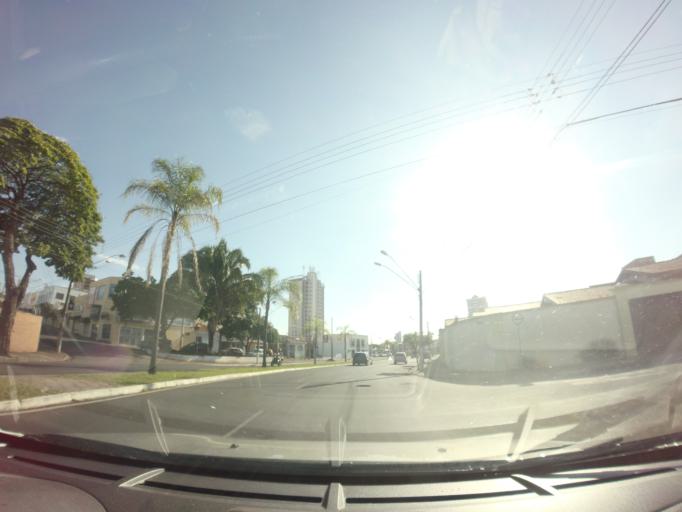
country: BR
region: Sao Paulo
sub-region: Rio Claro
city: Rio Claro
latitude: -22.4108
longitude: -47.5667
